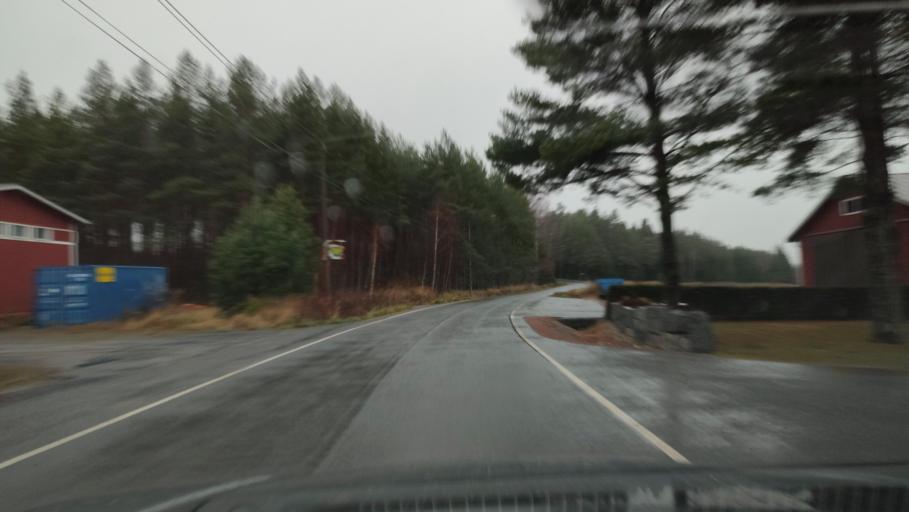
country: FI
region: Southern Ostrobothnia
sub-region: Suupohja
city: Karijoki
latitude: 62.1340
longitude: 21.6737
